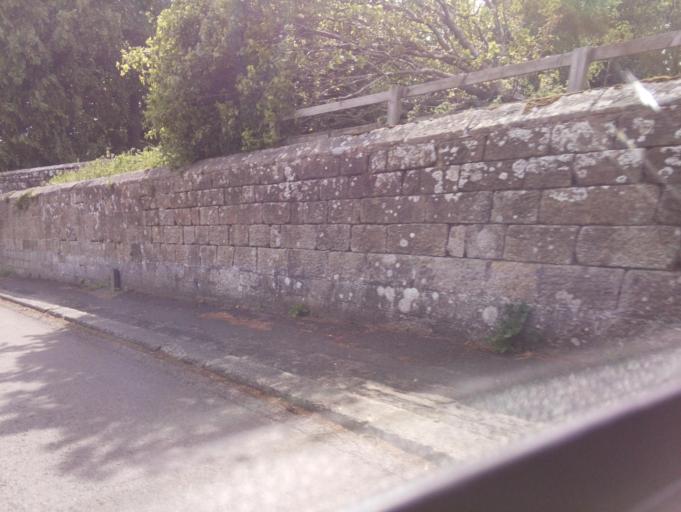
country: GB
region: England
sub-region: Northumberland
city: Alnwick
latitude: 55.4197
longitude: -1.7071
